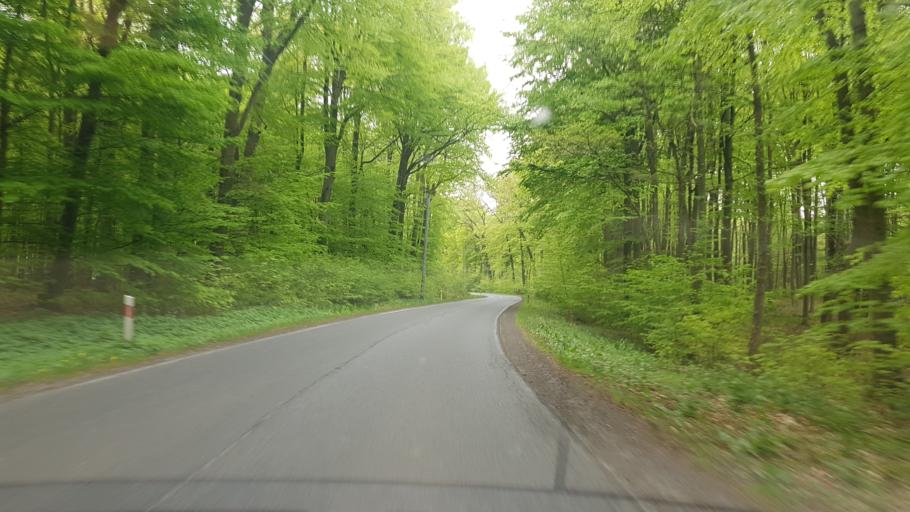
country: PL
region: West Pomeranian Voivodeship
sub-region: Powiat gryfinski
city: Stare Czarnowo
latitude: 53.2859
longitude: 14.7452
